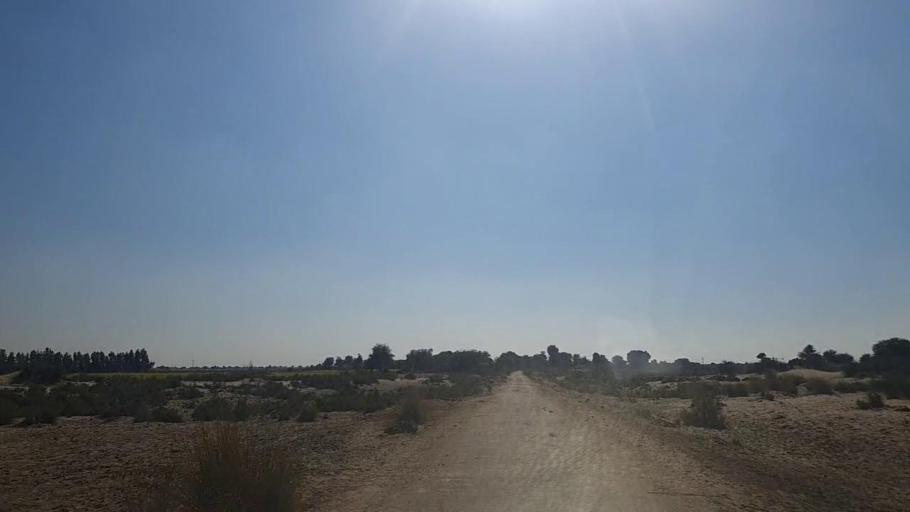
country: PK
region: Sindh
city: Khadro
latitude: 26.1578
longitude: 68.8380
